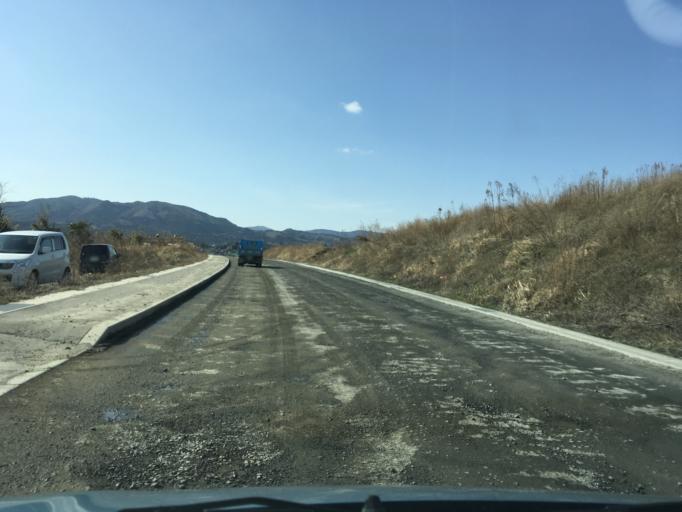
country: JP
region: Iwate
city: Ofunato
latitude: 38.8264
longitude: 141.5872
